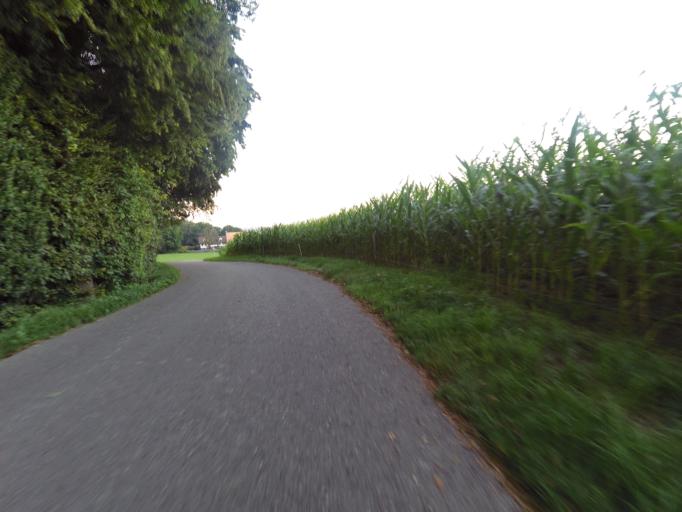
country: CH
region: Thurgau
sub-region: Weinfelden District
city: Wigoltingen
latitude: 47.5675
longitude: 9.0420
